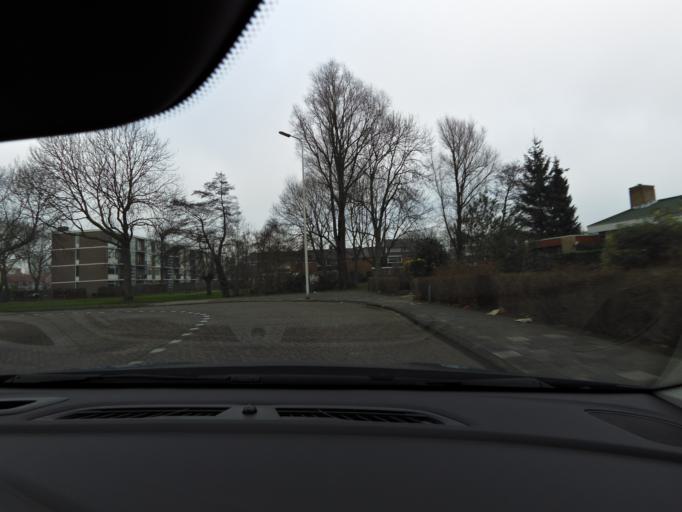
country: NL
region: South Holland
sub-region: Gemeente Spijkenisse
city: Spijkenisse
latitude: 51.8577
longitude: 4.3241
